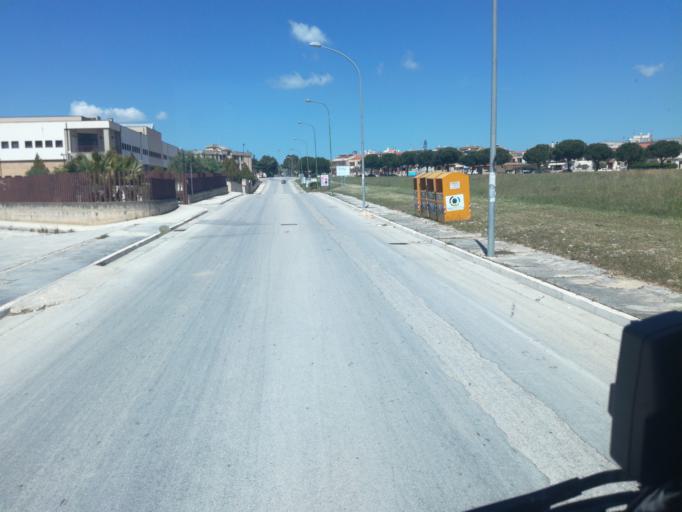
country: IT
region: Sicily
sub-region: Agrigento
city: Menfi
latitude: 37.6082
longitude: 12.9738
